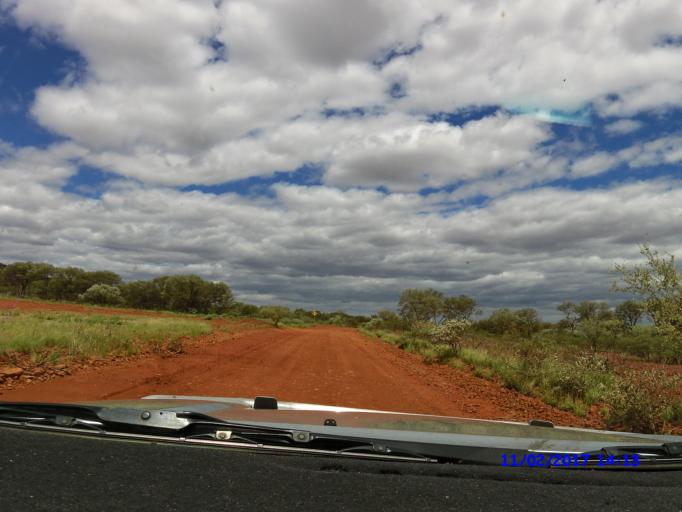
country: AU
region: Western Australia
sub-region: Ashburton
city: Tom Price
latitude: -23.0262
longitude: 117.9082
